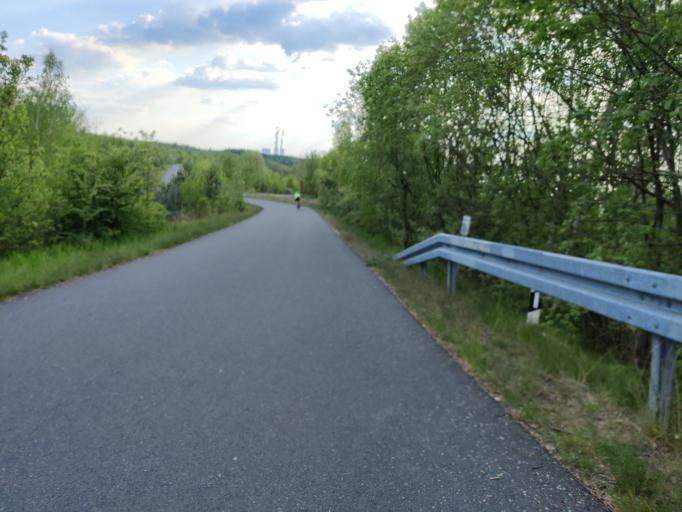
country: DE
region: Saxony
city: Grossposna
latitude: 51.2360
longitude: 12.4830
